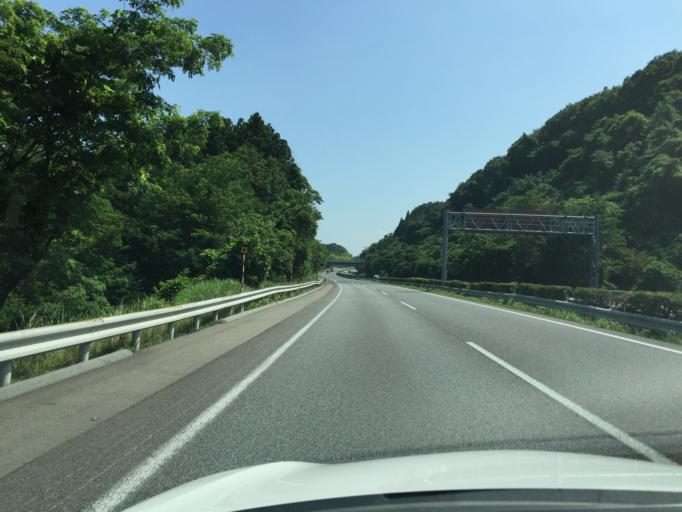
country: JP
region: Fukushima
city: Iwaki
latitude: 37.0306
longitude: 140.8143
